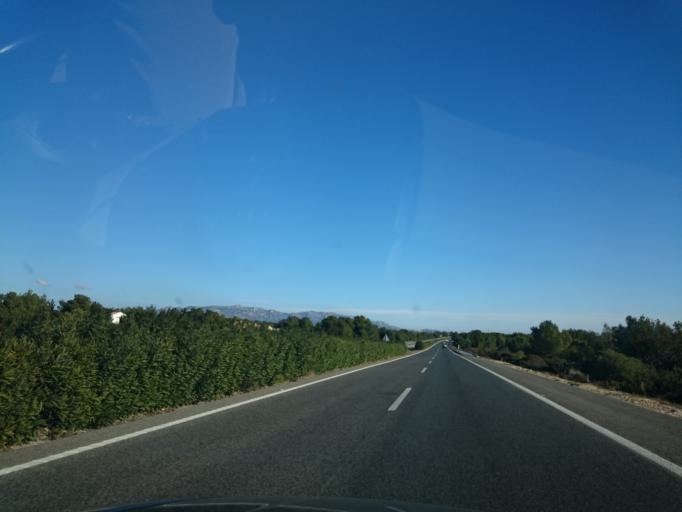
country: ES
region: Catalonia
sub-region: Provincia de Tarragona
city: El Perello
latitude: 40.8551
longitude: 0.7636
